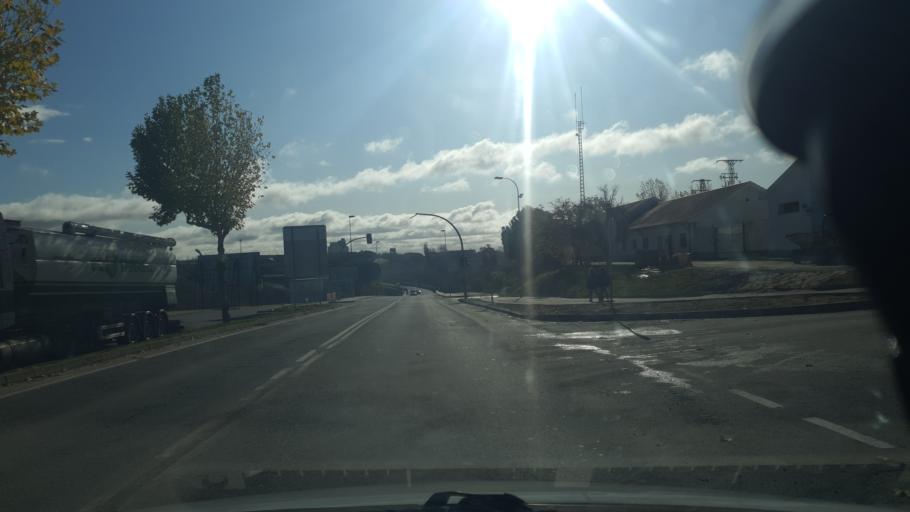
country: ES
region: Castille and Leon
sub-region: Provincia de Avila
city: Arevalo
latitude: 41.0526
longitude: -4.7092
